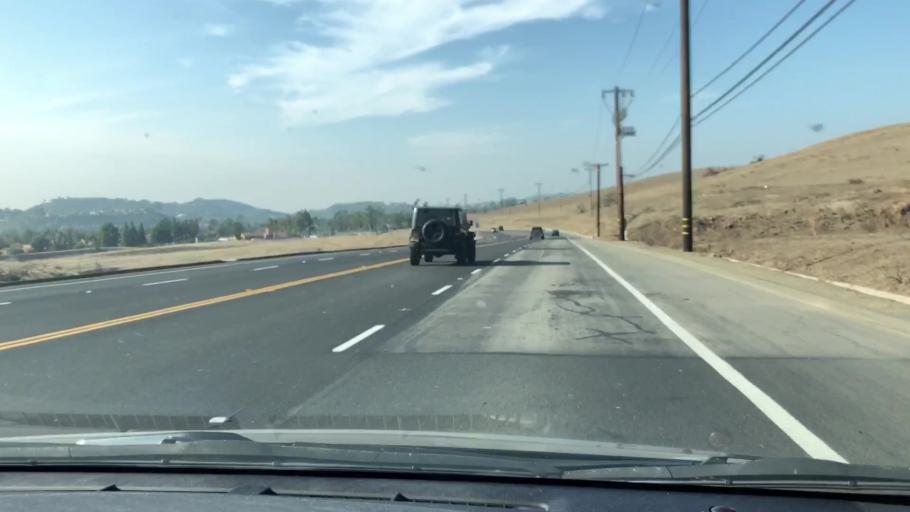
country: US
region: California
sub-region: Orange County
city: North Tustin
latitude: 33.7898
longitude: -117.7555
